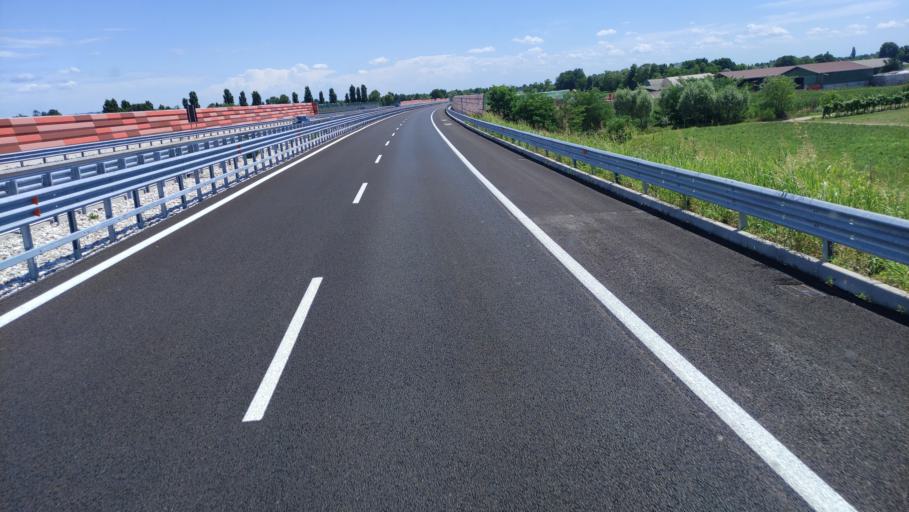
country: IT
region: Veneto
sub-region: Provincia di Treviso
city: Villa d'Asolo
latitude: 45.7548
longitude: 11.8830
